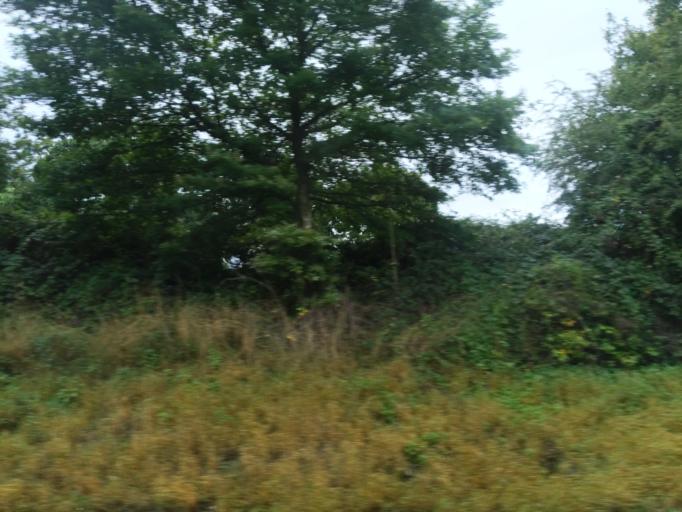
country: GB
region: England
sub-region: Kent
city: Sevenoaks
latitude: 51.2202
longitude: 0.2142
